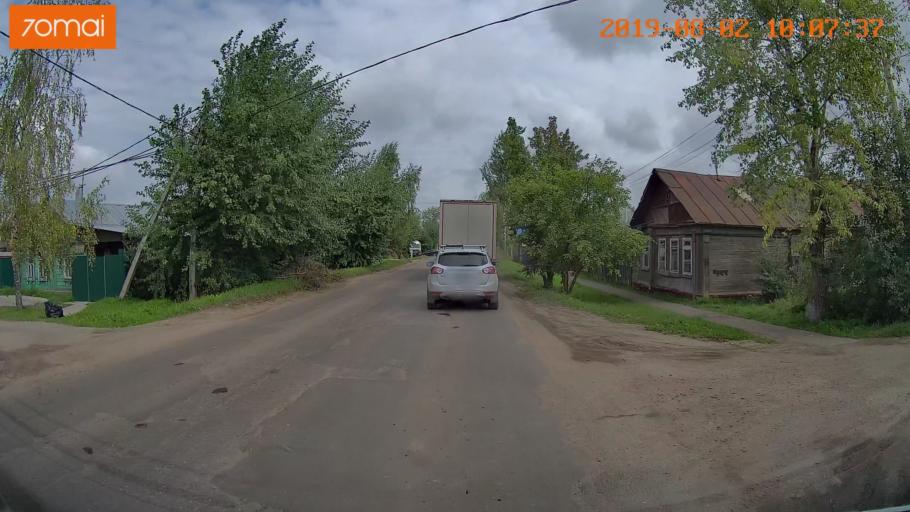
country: RU
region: Ivanovo
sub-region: Gorod Ivanovo
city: Ivanovo
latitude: 56.9830
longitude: 40.9362
